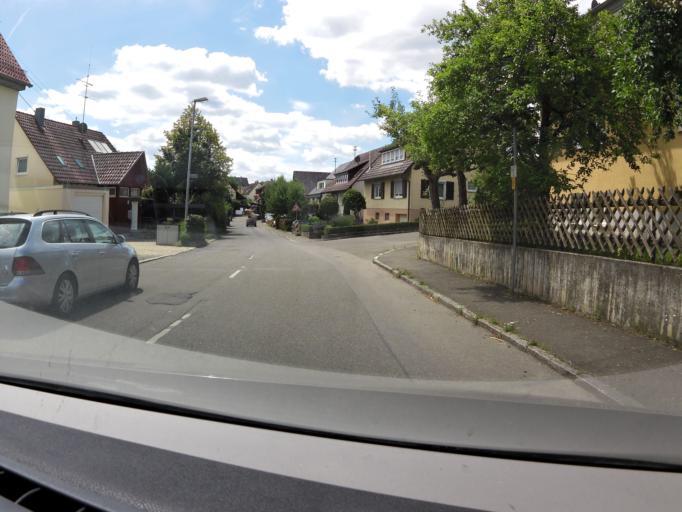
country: DE
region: Baden-Wuerttemberg
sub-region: Tuebingen Region
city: Tuebingen
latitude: 48.5428
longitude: 9.0095
